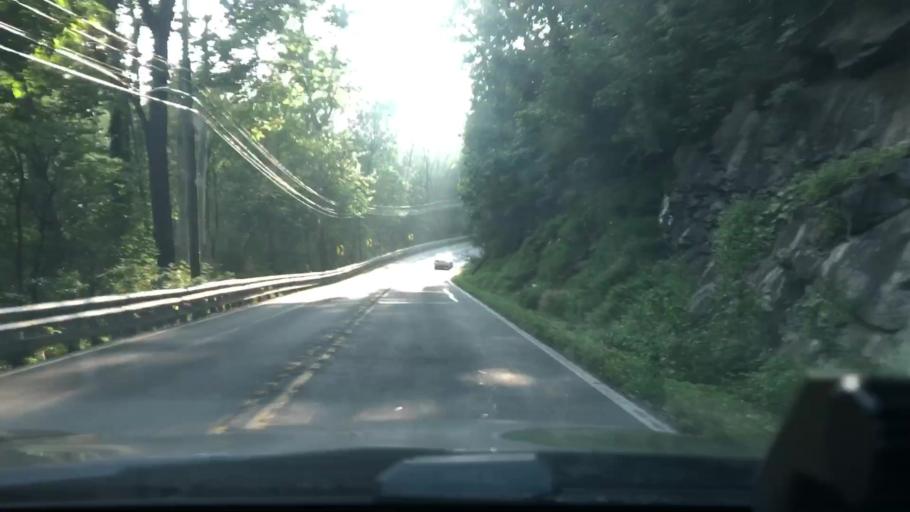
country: US
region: Pennsylvania
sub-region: Berks County
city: Kutztown
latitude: 40.5377
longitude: -75.7974
